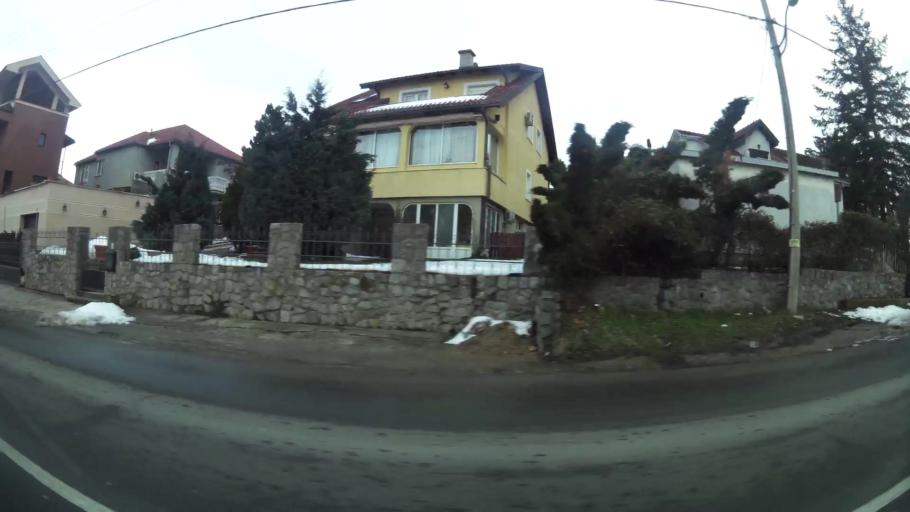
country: RS
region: Central Serbia
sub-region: Belgrade
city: Vozdovac
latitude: 44.7372
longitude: 20.4855
